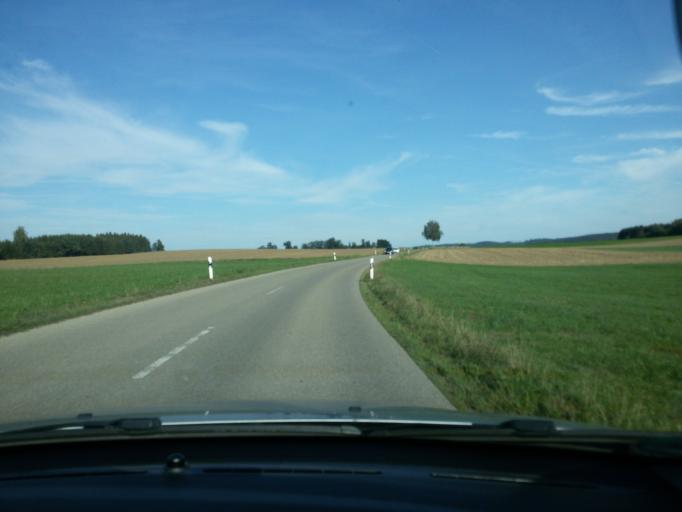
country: DE
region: Bavaria
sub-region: Swabia
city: Kutzenhausen
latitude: 48.3433
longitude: 10.7125
